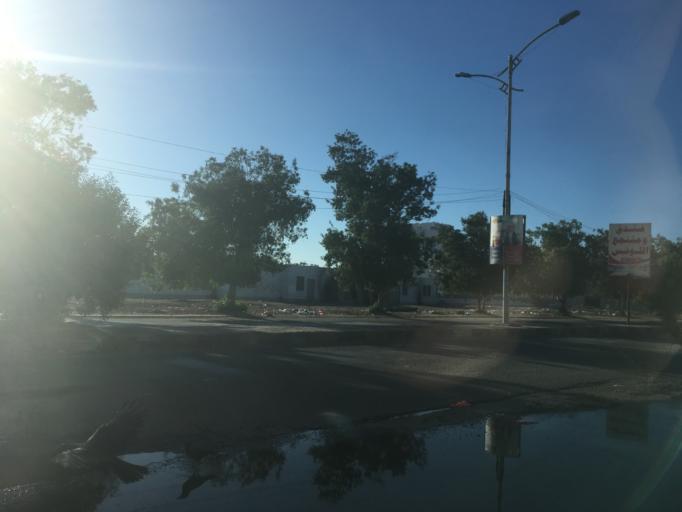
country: YE
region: Aden
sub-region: Khur Maksar
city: Khawr Maksar
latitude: 12.8111
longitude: 45.0416
